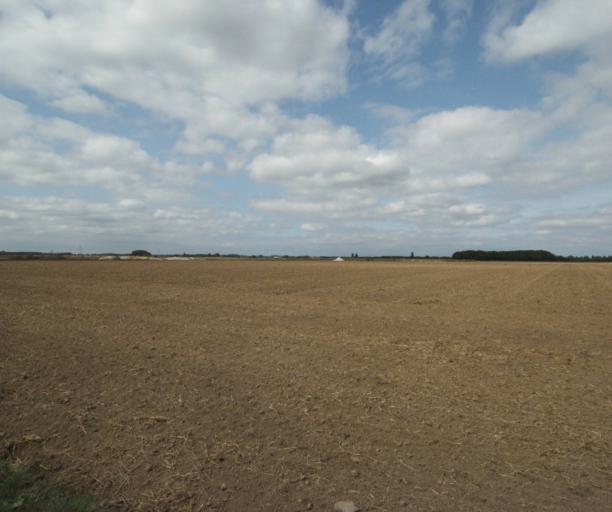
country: FR
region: Nord-Pas-de-Calais
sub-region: Departement du Nord
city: Baisieux
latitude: 50.5964
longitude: 3.2375
